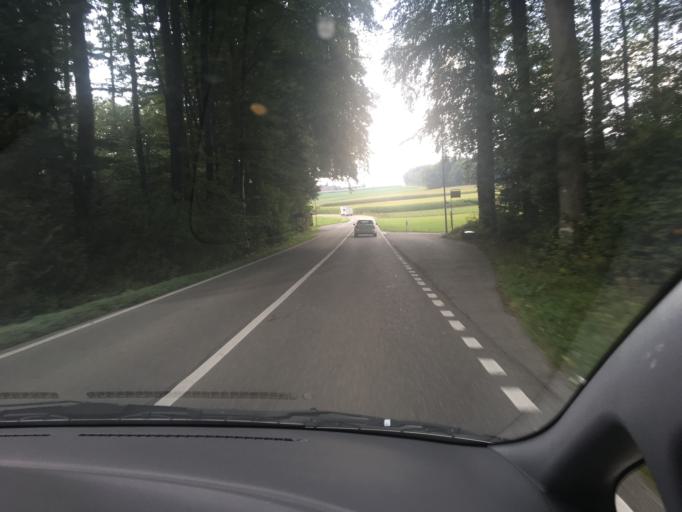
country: CH
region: Bern
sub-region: Seeland District
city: Schupfen
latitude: 47.0050
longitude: 7.3836
